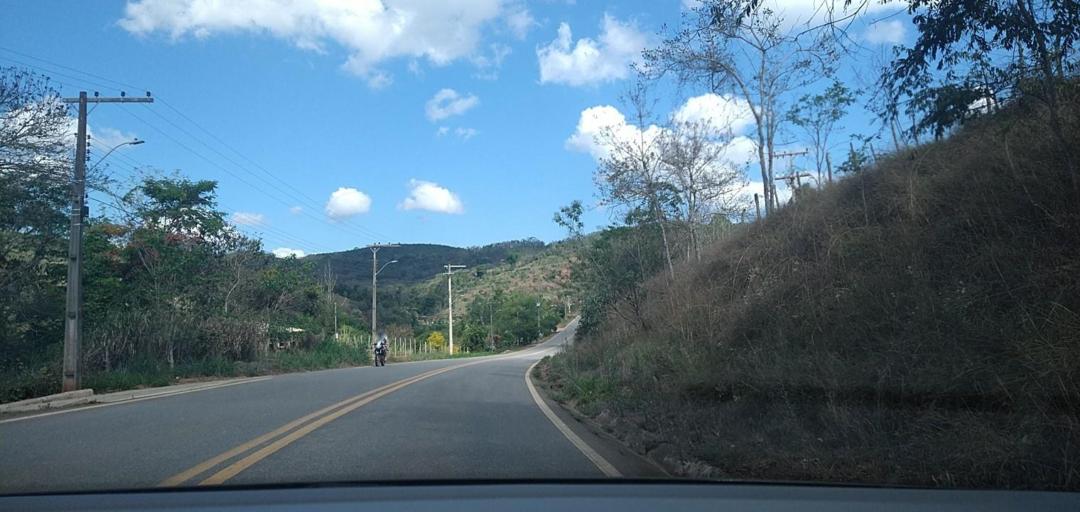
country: BR
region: Minas Gerais
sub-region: Rio Piracicaba
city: Rio Piracicaba
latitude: -20.0032
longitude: -43.1008
